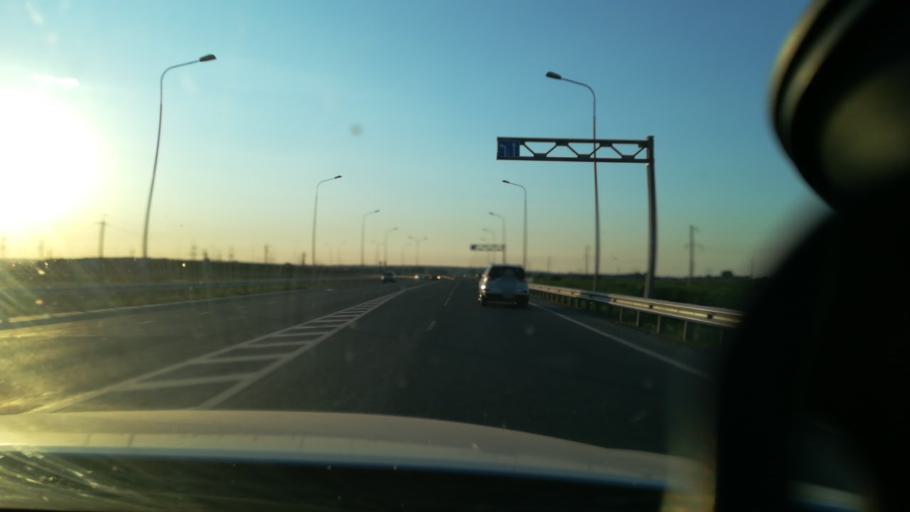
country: RU
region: Krasnodarskiy
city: Dzhiginka
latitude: 45.1347
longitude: 37.3215
